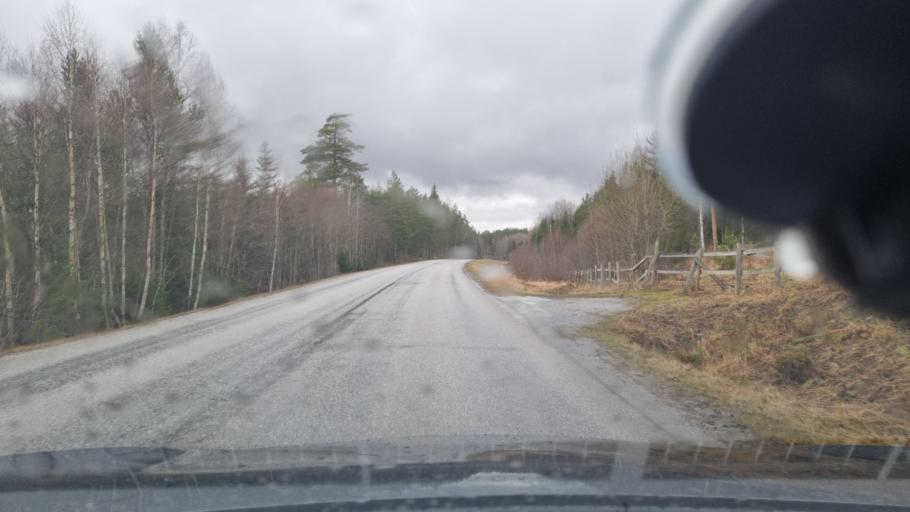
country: SE
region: Stockholm
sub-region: Sigtuna Kommun
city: Sigtuna
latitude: 59.5545
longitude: 17.7260
